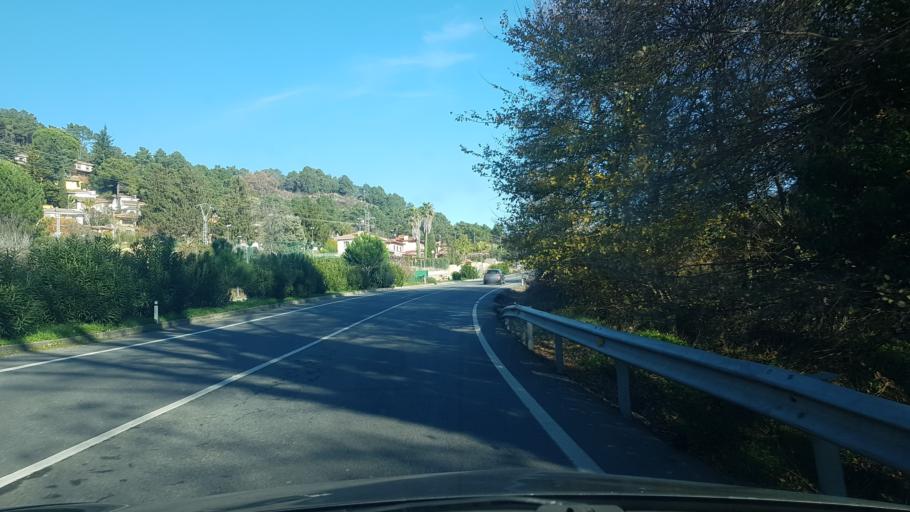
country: ES
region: Castille and Leon
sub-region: Provincia de Avila
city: Casillas
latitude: 40.3041
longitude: -4.5382
